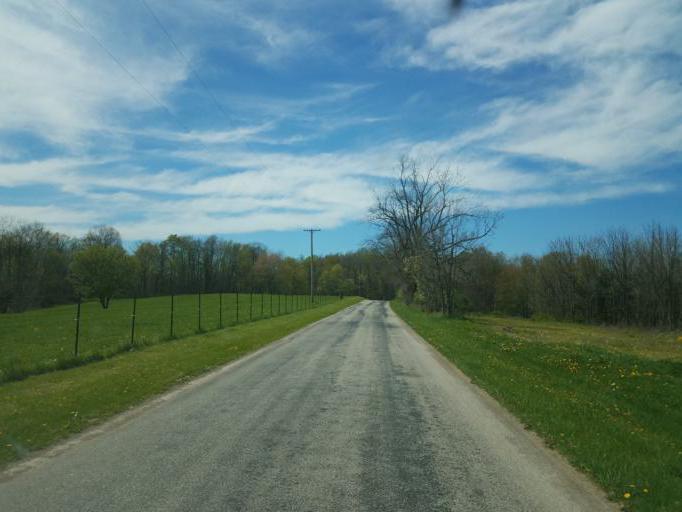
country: US
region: Ohio
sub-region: Richland County
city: Lincoln Heights
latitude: 40.8967
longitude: -82.5203
